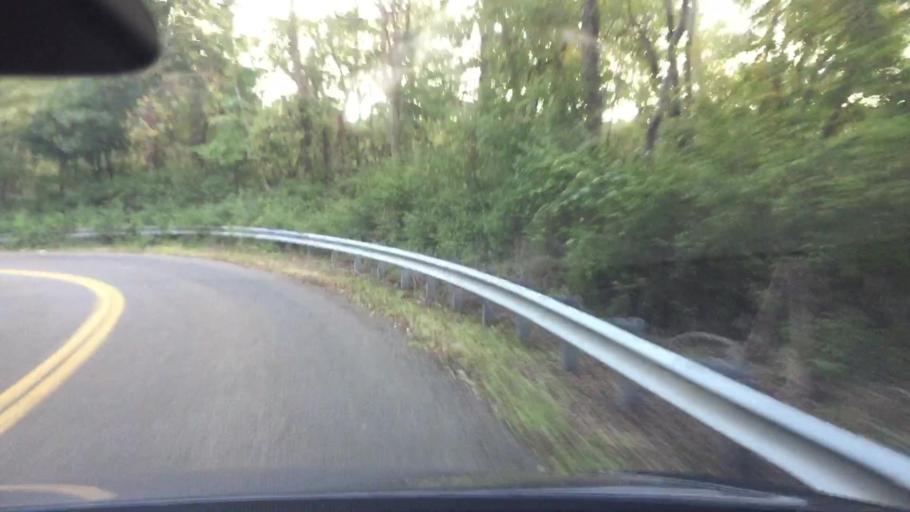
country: US
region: Pennsylvania
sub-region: Allegheny County
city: Bakerstown
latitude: 40.6241
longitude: -79.9064
